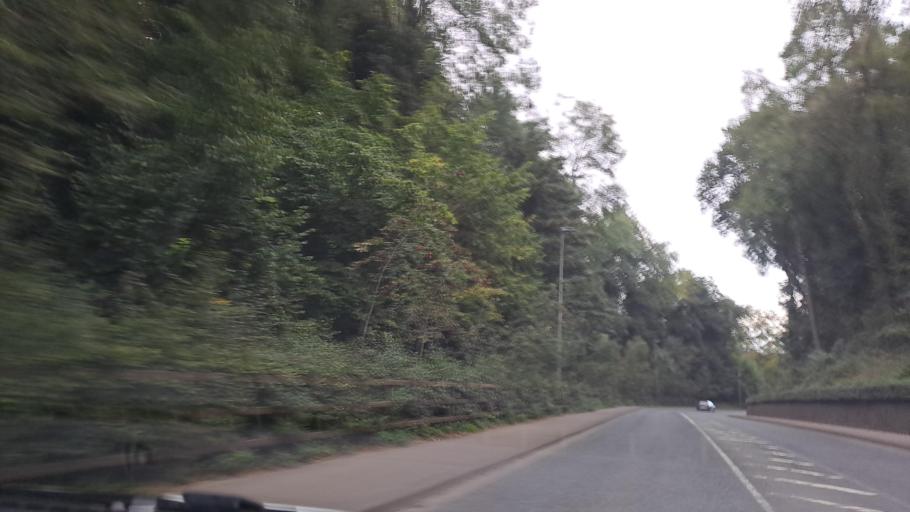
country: IE
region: Ulster
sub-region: County Monaghan
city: Monaghan
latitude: 54.2405
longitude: -6.9696
